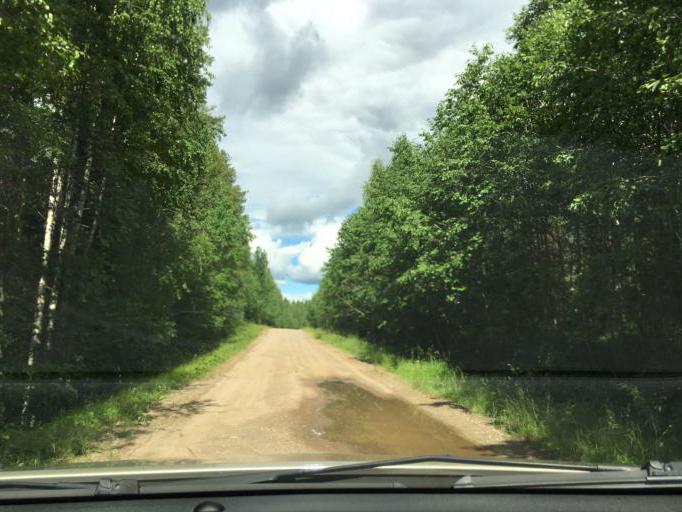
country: SE
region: Norrbotten
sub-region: Overkalix Kommun
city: OEverkalix
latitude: 66.1571
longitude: 22.8575
